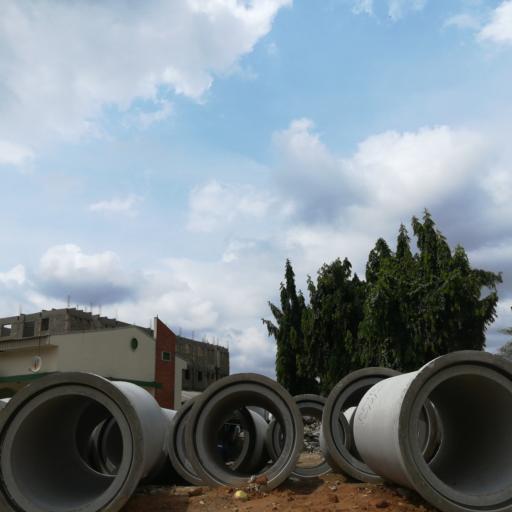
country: NG
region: Rivers
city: Port Harcourt
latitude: 4.8509
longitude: 7.0630
